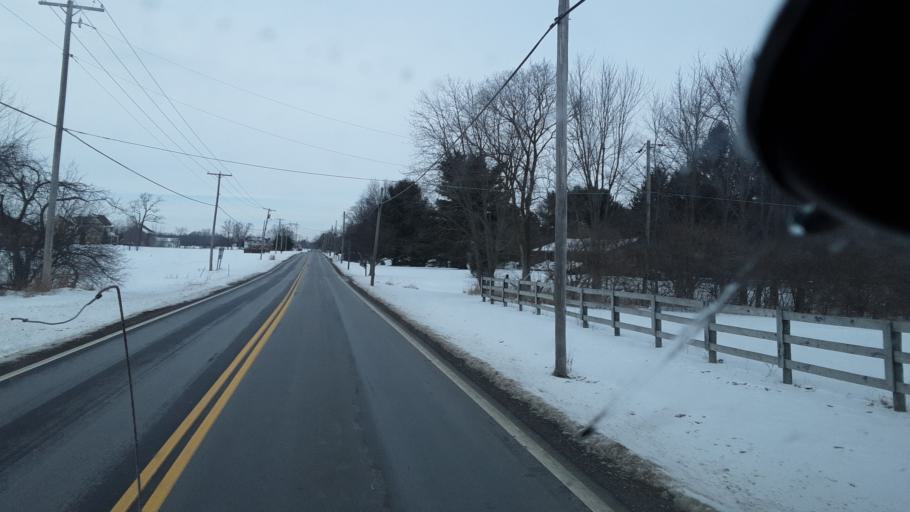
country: US
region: Ohio
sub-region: Delaware County
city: Powell
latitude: 40.2206
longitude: -83.1495
